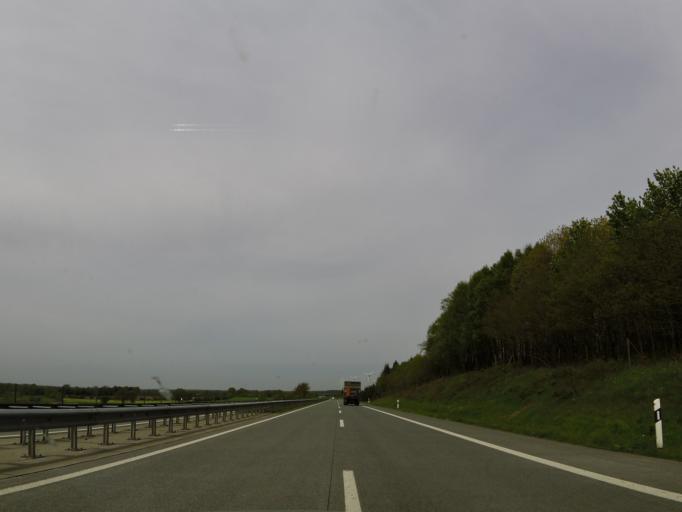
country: DE
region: Schleswig-Holstein
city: Nienbuttel
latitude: 54.0450
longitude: 9.4073
